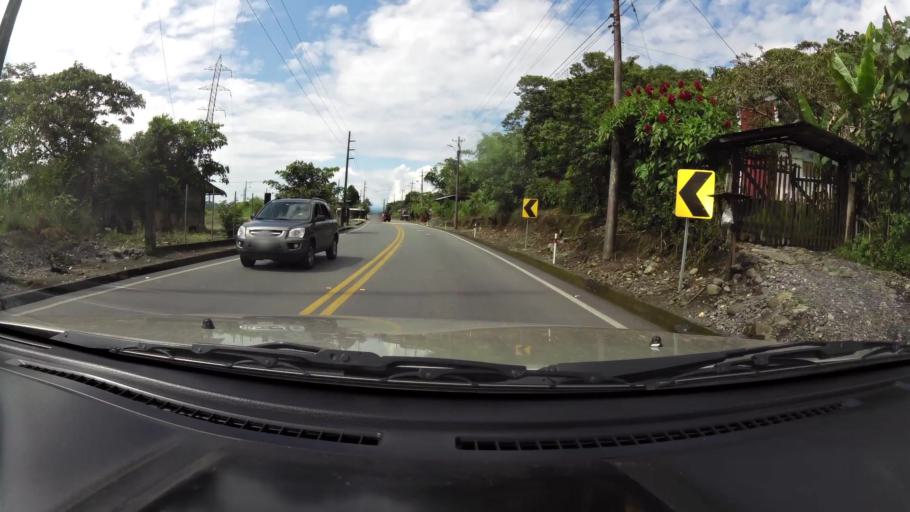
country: EC
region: Pastaza
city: Puyo
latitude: -1.4892
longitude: -78.0160
